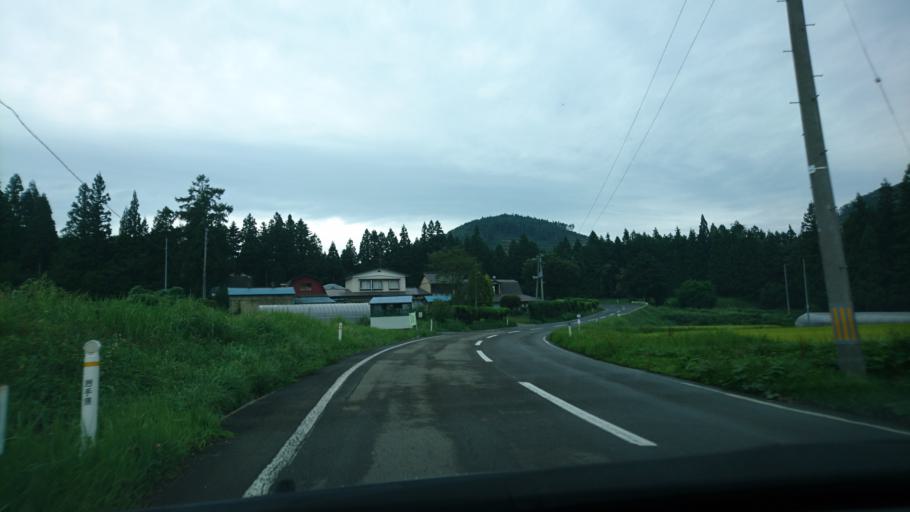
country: JP
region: Iwate
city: Mizusawa
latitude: 39.0267
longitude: 141.2028
